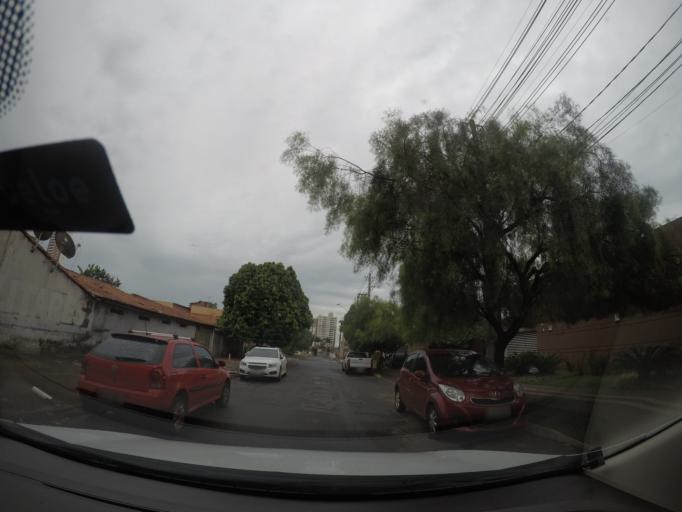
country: BR
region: Goias
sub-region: Goiania
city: Goiania
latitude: -16.6824
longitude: -49.2370
